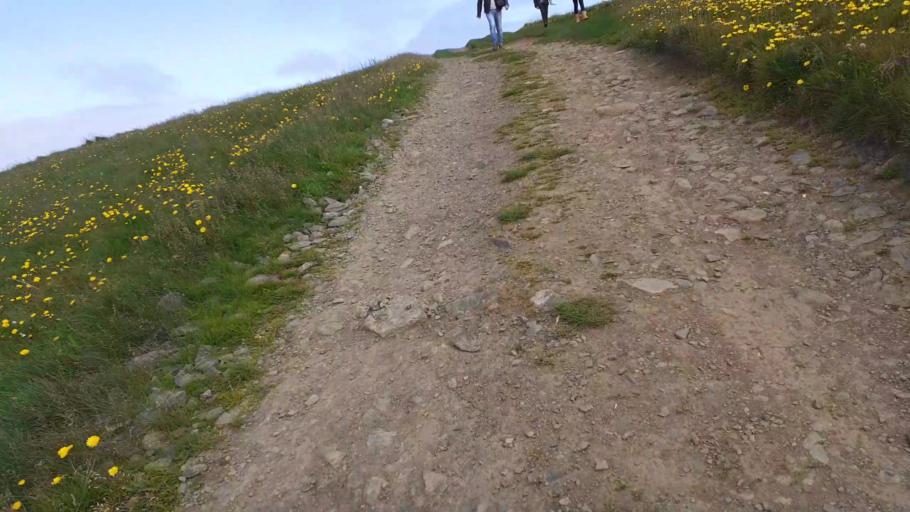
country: IS
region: Northeast
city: Dalvik
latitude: 66.5526
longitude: -18.0158
